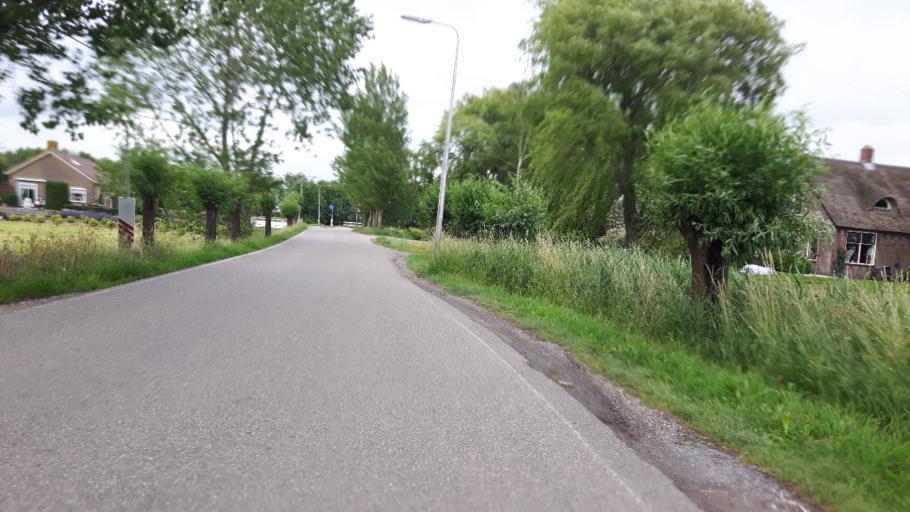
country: NL
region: Utrecht
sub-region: Gemeente Woerden
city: Woerden
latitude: 52.0747
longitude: 4.8240
